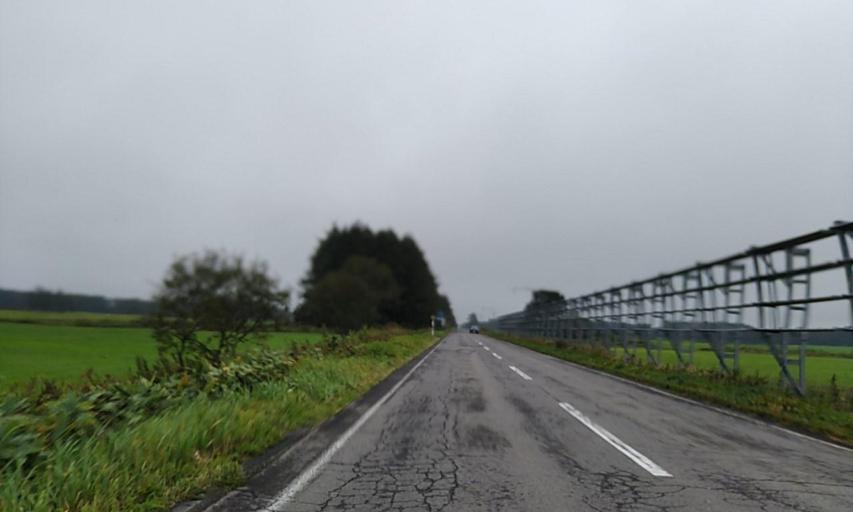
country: JP
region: Hokkaido
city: Shibetsu
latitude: 43.5275
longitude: 144.6953
